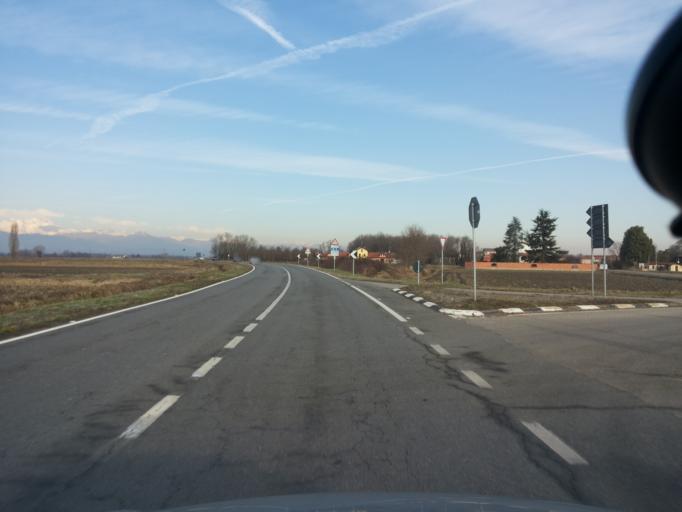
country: IT
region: Piedmont
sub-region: Provincia di Vercelli
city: Albano Vercellese
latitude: 45.4202
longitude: 8.3796
